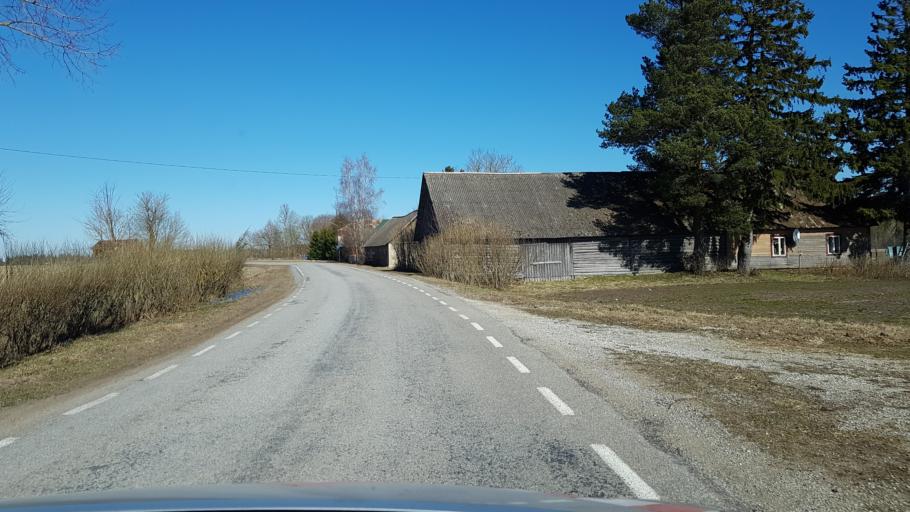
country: EE
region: Laeaene-Virumaa
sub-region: Someru vald
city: Someru
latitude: 59.3955
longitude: 26.5004
